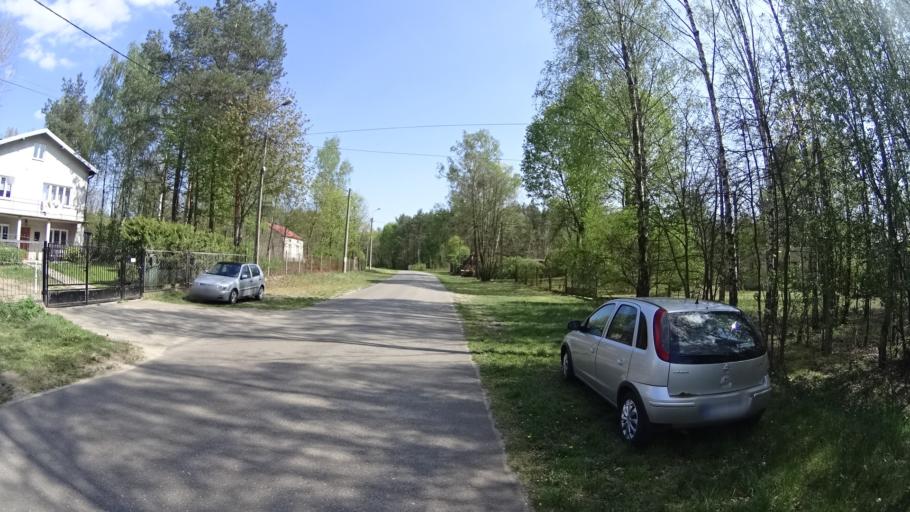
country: PL
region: Masovian Voivodeship
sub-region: Powiat warszawski zachodni
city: Izabelin
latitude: 52.3157
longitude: 20.8020
